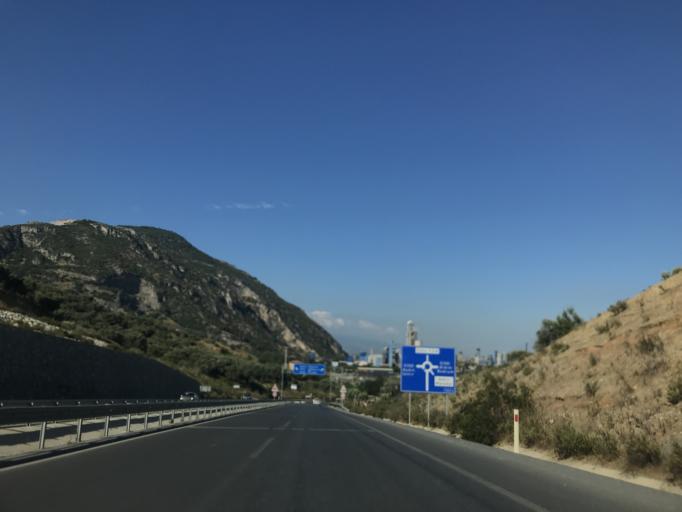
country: TR
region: Aydin
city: Soeke
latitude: 37.7662
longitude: 27.4191
